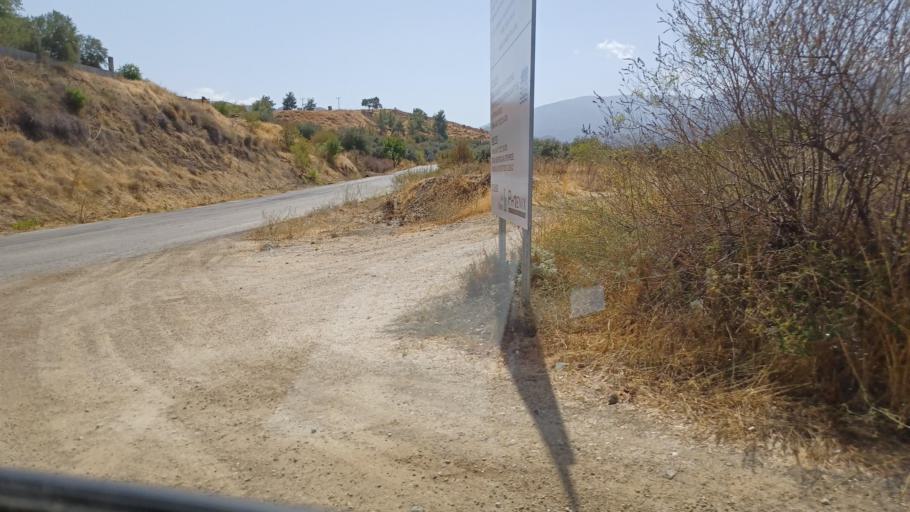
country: CY
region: Lefkosia
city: Kakopetria
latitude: 35.0551
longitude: 32.8920
